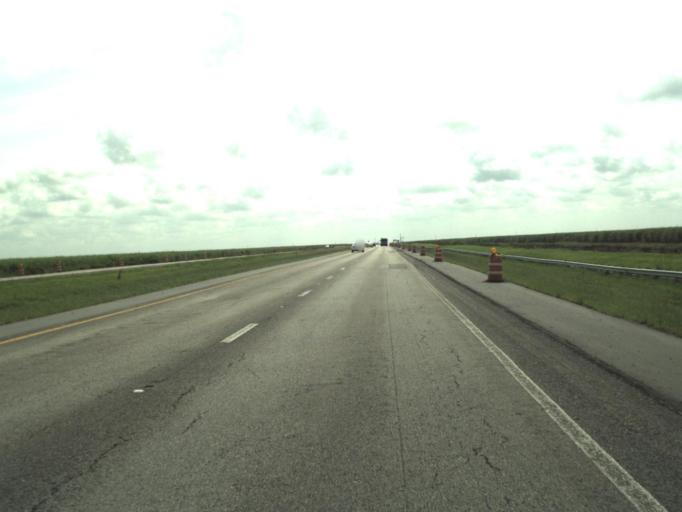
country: US
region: Florida
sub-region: Palm Beach County
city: Belle Glade
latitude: 26.7260
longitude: -80.5939
